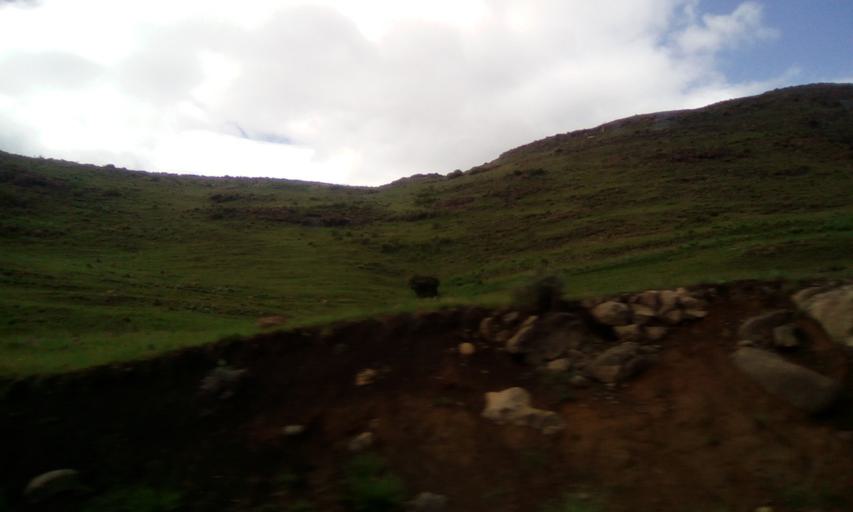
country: LS
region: Maseru
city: Nako
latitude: -29.6575
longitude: 27.8717
